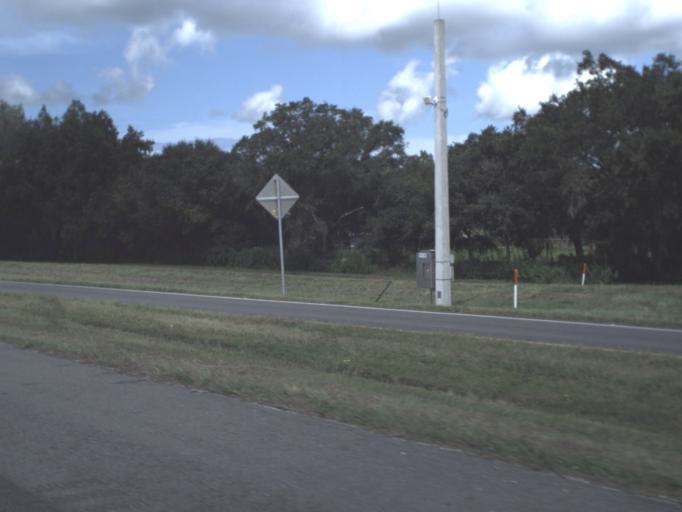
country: US
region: Florida
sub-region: Sarasota County
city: Plantation
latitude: 27.1100
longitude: -82.3519
